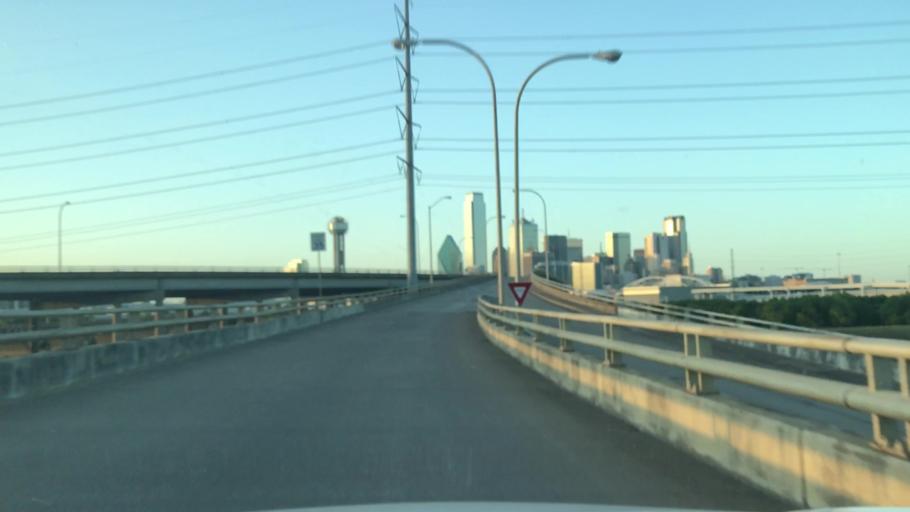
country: US
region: Texas
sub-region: Dallas County
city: Dallas
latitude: 32.7619
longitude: -96.8128
